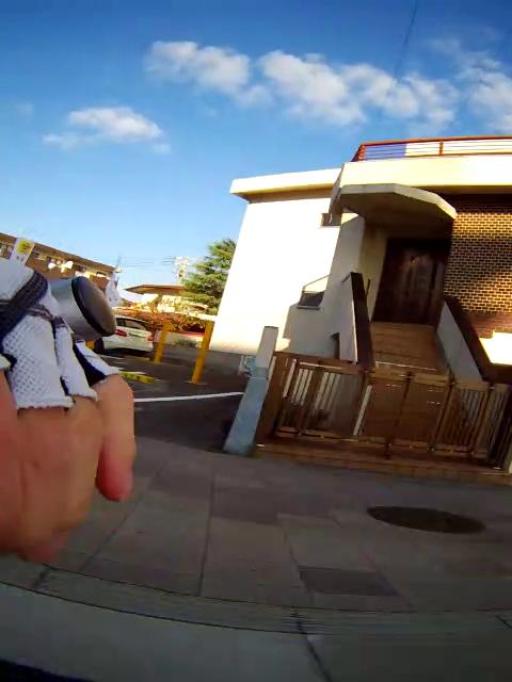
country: JP
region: Hyogo
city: Takarazuka
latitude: 34.7733
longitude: 135.3592
